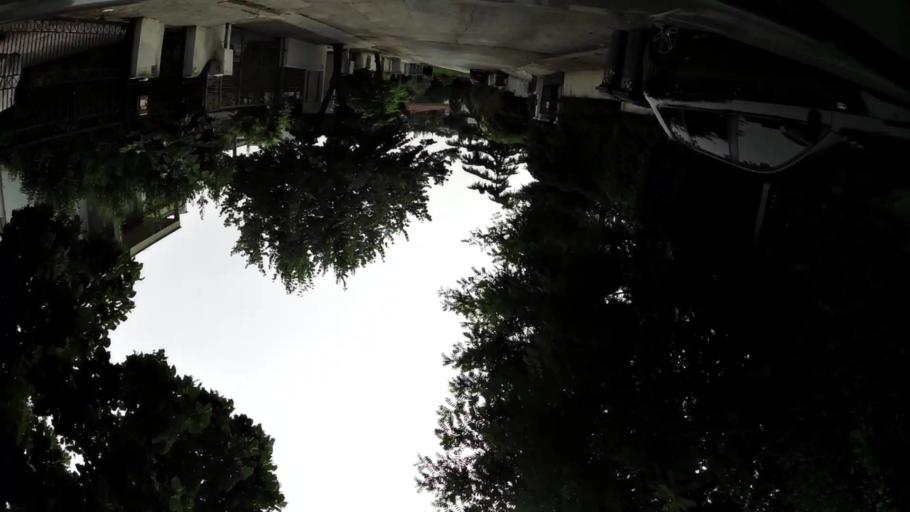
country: GR
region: Central Macedonia
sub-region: Nomos Thessalonikis
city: Panorama
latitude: 40.5862
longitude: 23.0189
